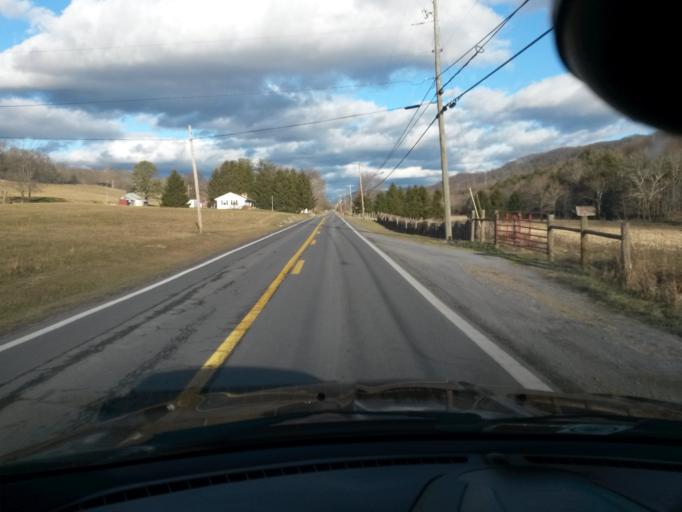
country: US
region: Virginia
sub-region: Giles County
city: Pearisburg
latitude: 37.4364
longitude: -80.6992
